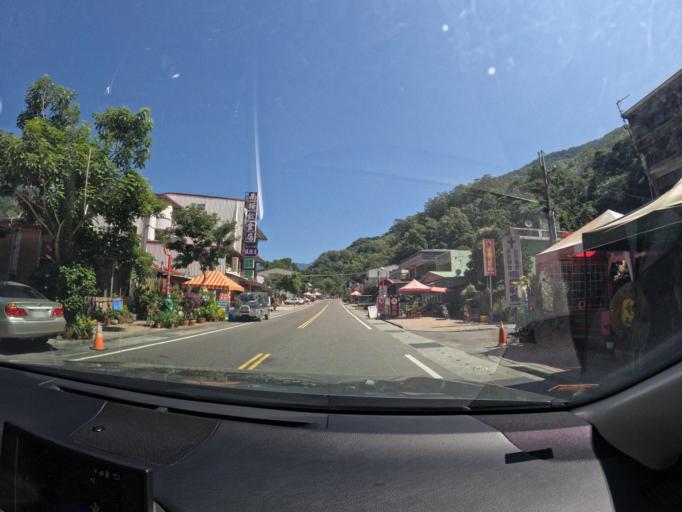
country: TW
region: Taiwan
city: Yujing
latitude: 23.2394
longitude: 120.8122
